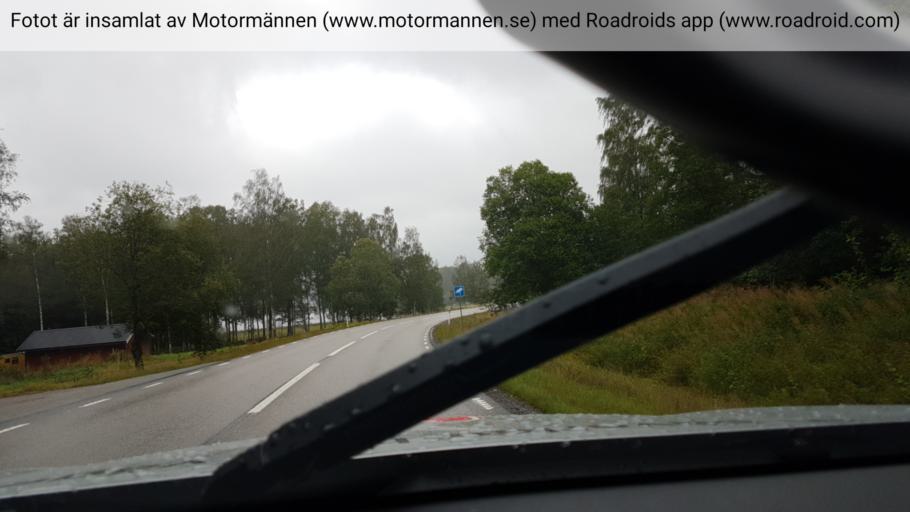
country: SE
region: Vaestra Goetaland
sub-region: Bengtsfors Kommun
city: Dals Langed
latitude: 58.8682
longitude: 12.1912
